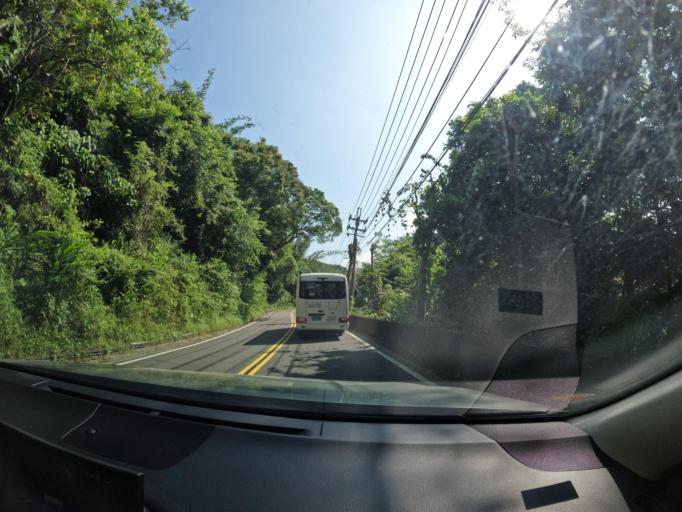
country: TW
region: Taiwan
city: Yujing
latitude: 23.0702
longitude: 120.6515
